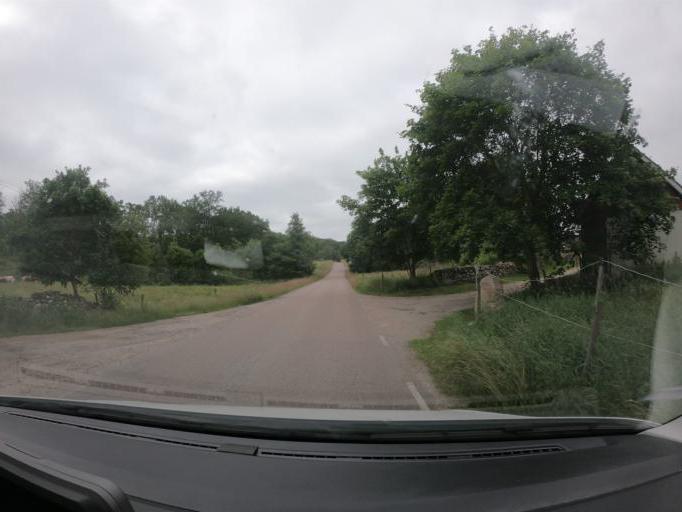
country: SE
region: Skane
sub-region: Perstorps Kommun
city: Perstorp
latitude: 56.1070
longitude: 13.3502
